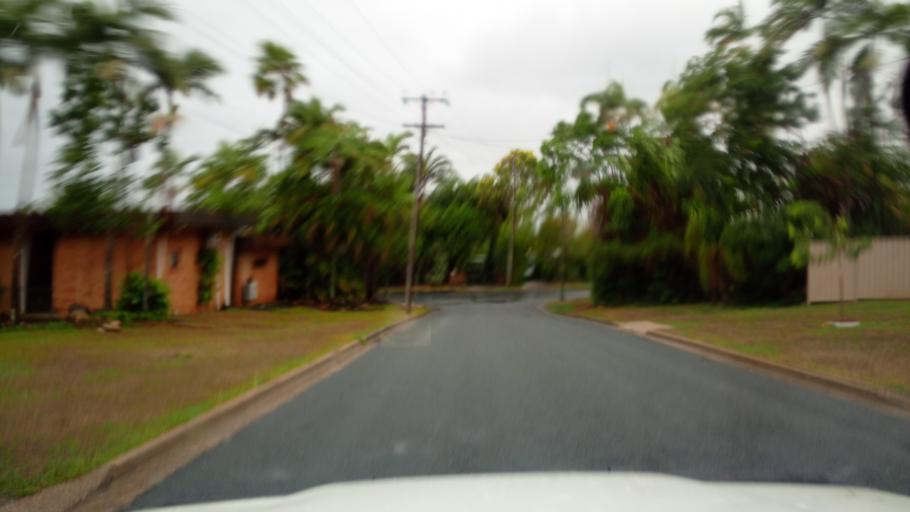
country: AU
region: Queensland
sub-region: Cairns
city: Woree
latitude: -16.9609
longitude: 145.7301
